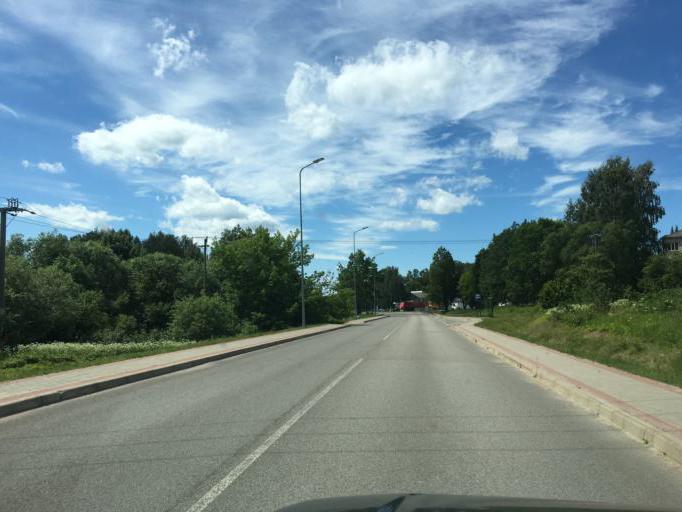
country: LV
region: Balvu Rajons
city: Balvi
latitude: 57.1389
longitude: 27.2617
